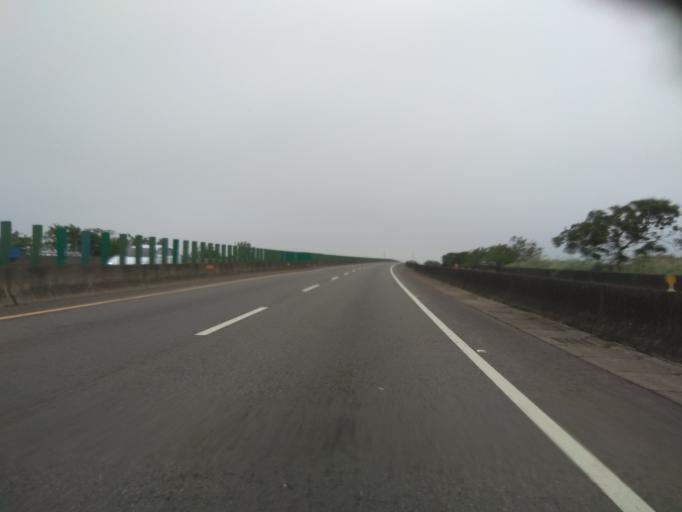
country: TW
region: Taiwan
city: Taoyuan City
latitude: 24.9749
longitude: 121.1340
